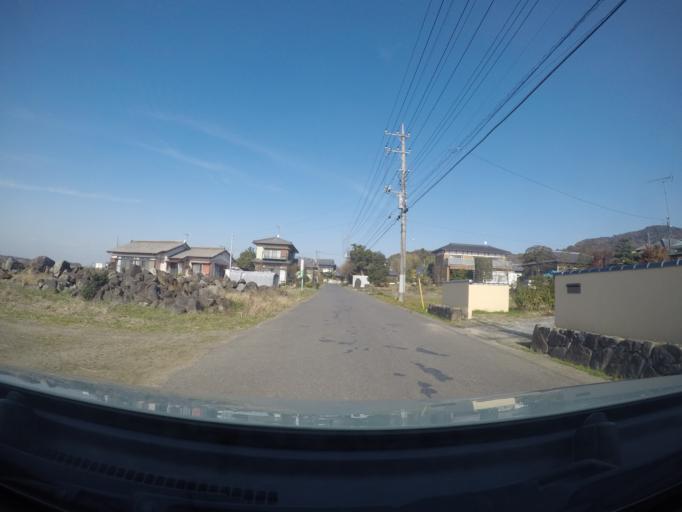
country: JP
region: Ibaraki
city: Tsukuba
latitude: 36.2311
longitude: 140.0656
